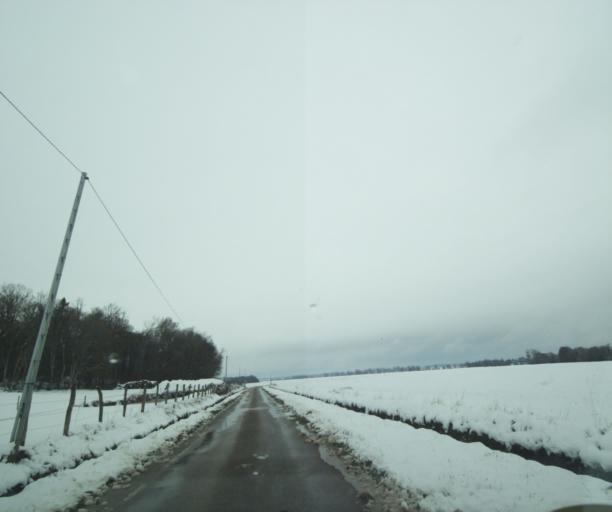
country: FR
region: Champagne-Ardenne
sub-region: Departement de la Haute-Marne
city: Montier-en-Der
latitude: 48.4266
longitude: 4.7888
